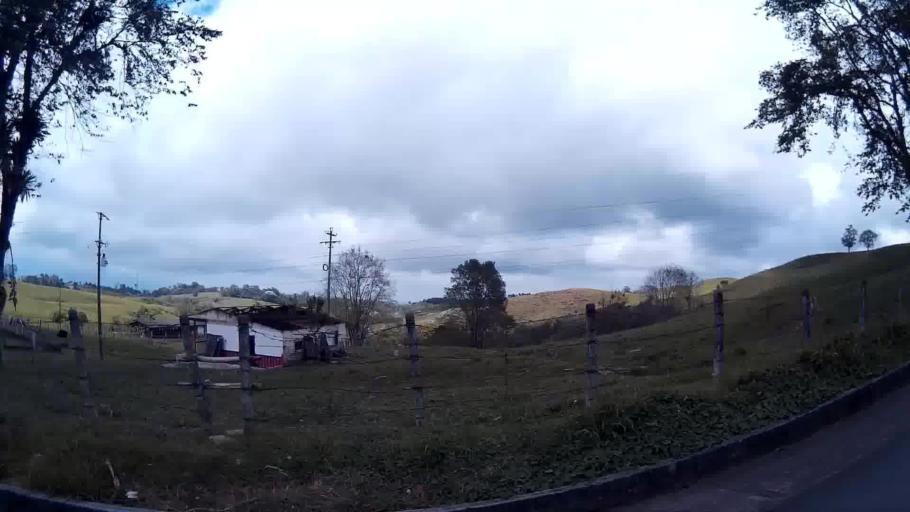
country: CO
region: Quindio
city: Salento
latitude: 4.6730
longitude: -75.5974
